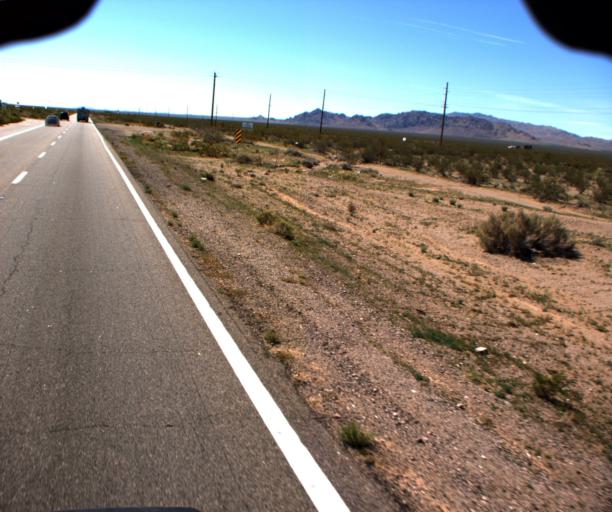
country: US
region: Arizona
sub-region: Mohave County
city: Dolan Springs
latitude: 35.7011
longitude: -114.4755
